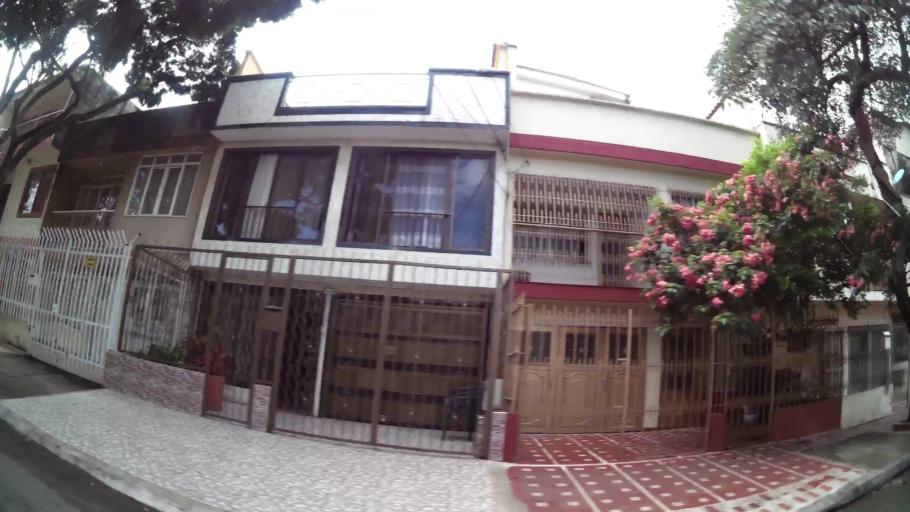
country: CO
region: Valle del Cauca
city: Cali
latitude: 3.3893
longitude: -76.5491
